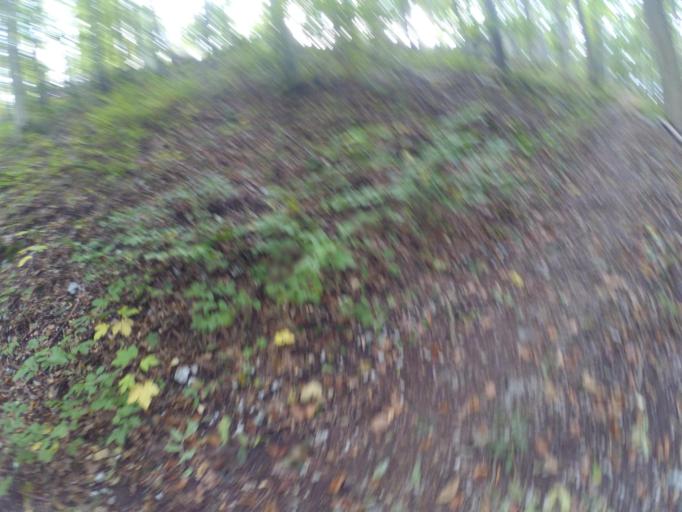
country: DE
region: Baden-Wuerttemberg
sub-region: Regierungsbezirk Stuttgart
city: Heubach
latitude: 48.7837
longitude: 9.9220
